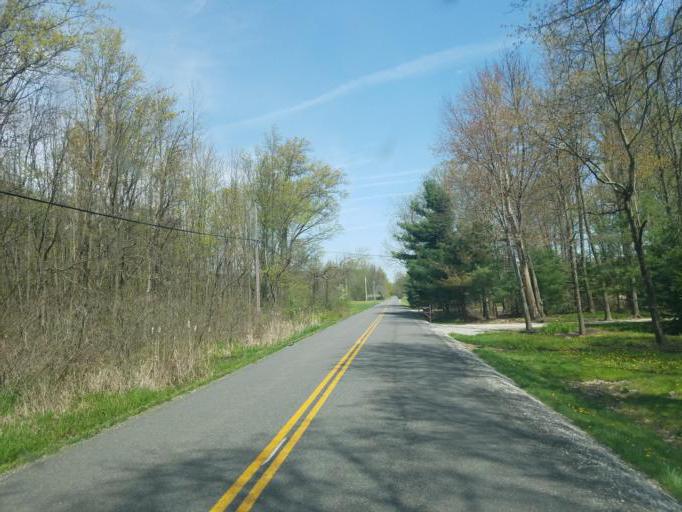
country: US
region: Ohio
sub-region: Medina County
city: Medina
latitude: 41.1420
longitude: -81.7748
